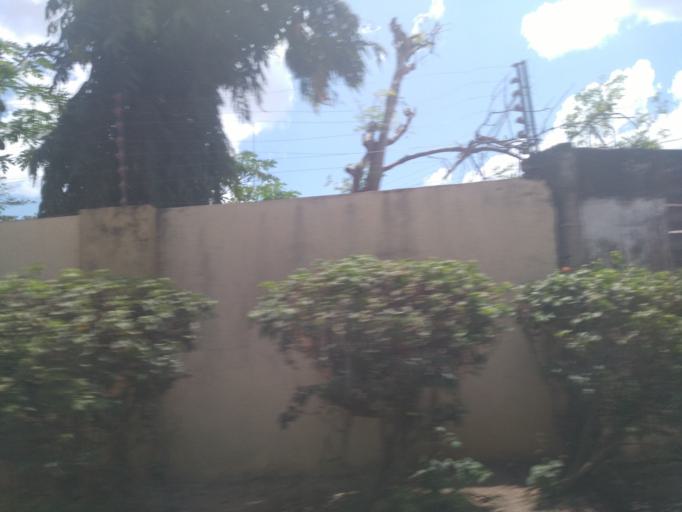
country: TZ
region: Dar es Salaam
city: Dar es Salaam
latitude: -6.8468
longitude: 39.2648
